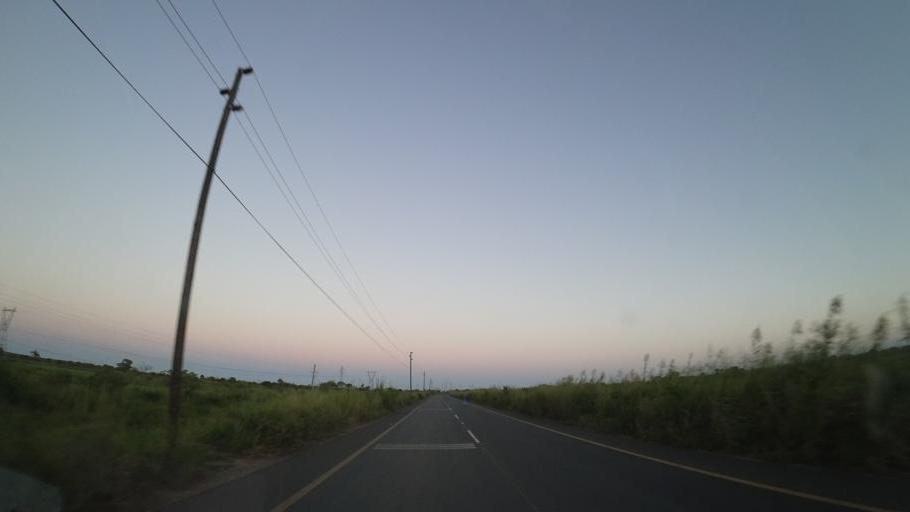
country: MZ
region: Sofala
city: Dondo
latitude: -19.5140
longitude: 34.6166
